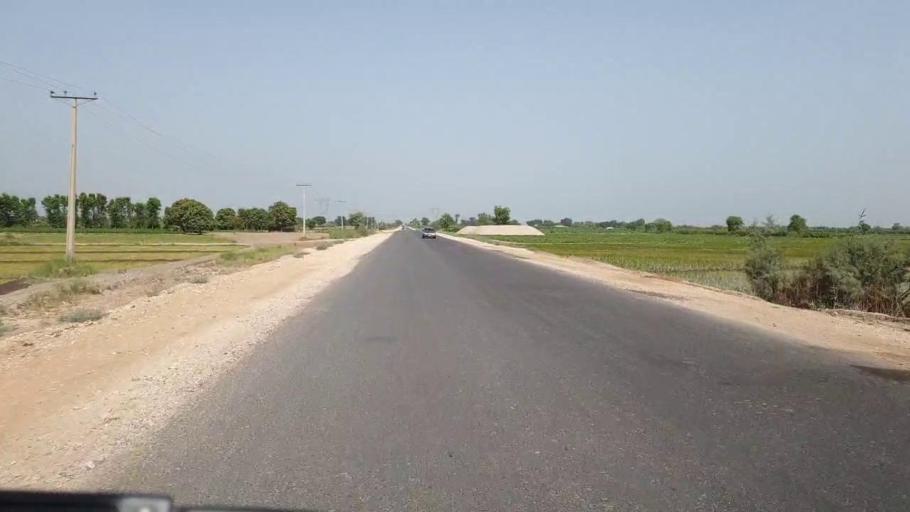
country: PK
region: Sindh
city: Sakrand
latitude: 26.2572
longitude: 68.1929
